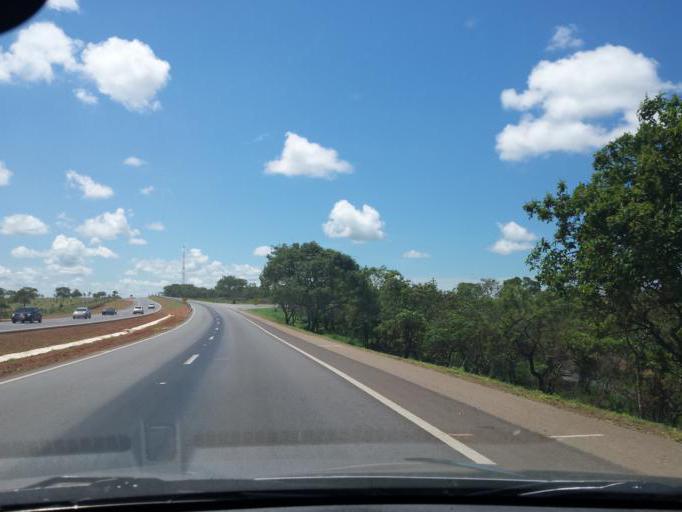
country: BR
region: Goias
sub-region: Luziania
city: Luziania
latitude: -16.3559
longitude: -47.8325
